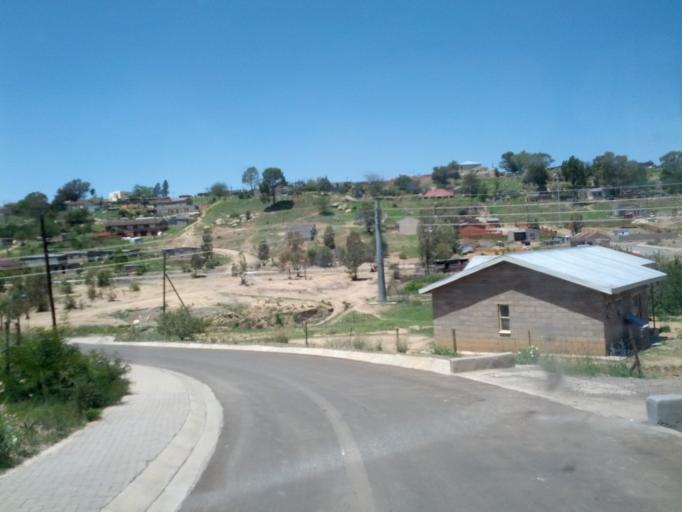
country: LS
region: Maseru
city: Maseru
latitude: -29.3069
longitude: 27.4891
